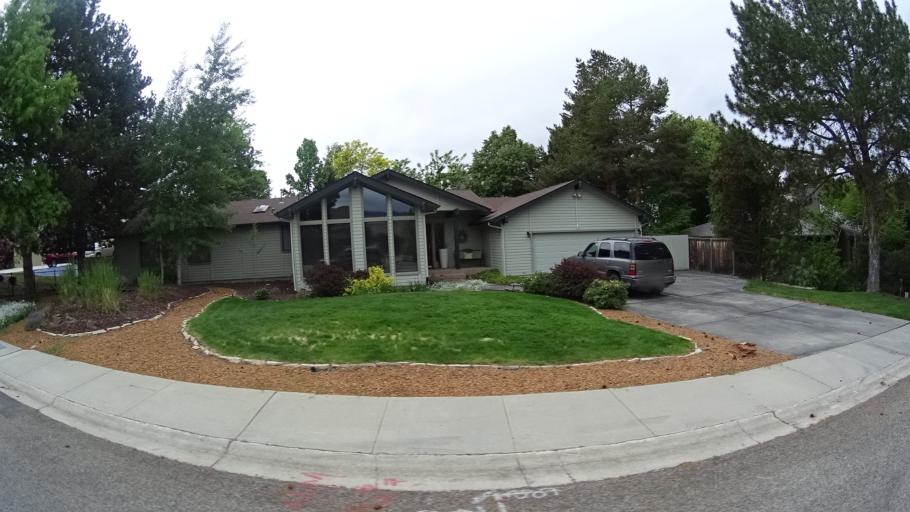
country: US
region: Idaho
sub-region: Ada County
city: Boise
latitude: 43.6151
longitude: -116.1609
